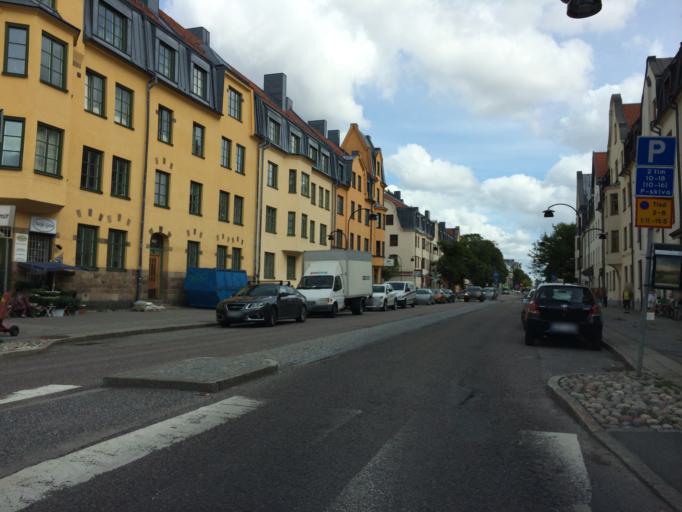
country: SE
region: Stockholm
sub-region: Stockholms Kommun
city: Arsta
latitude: 59.3054
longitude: 17.9981
